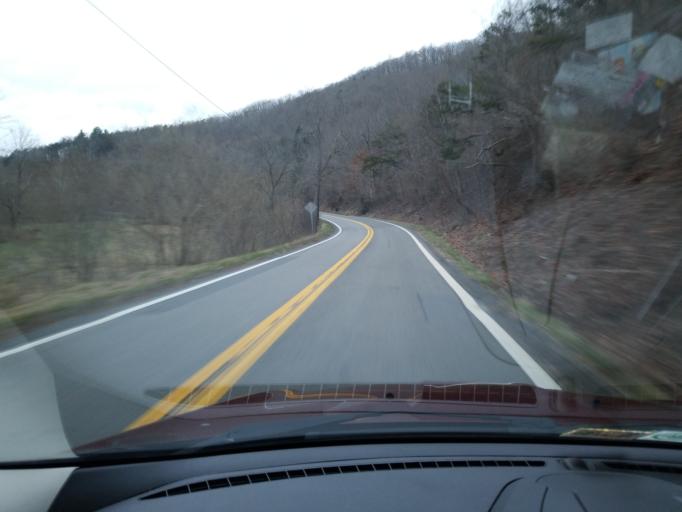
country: US
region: West Virginia
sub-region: Monroe County
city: Union
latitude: 37.5273
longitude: -80.6067
